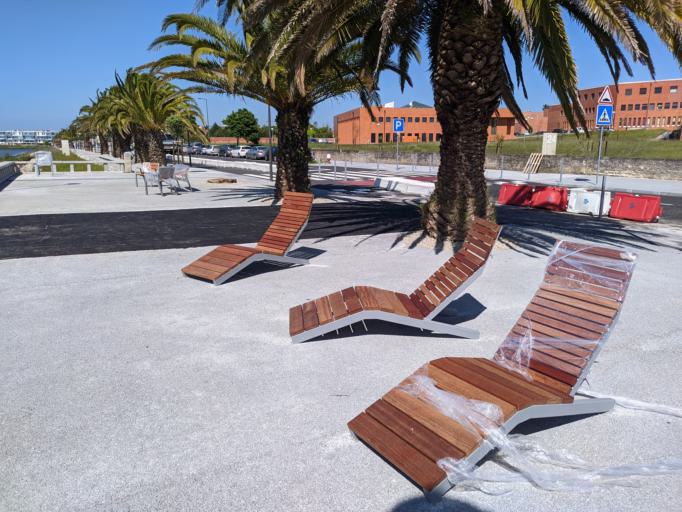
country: PT
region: Aveiro
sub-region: Aveiro
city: Aveiro
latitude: 40.6335
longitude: -8.6615
